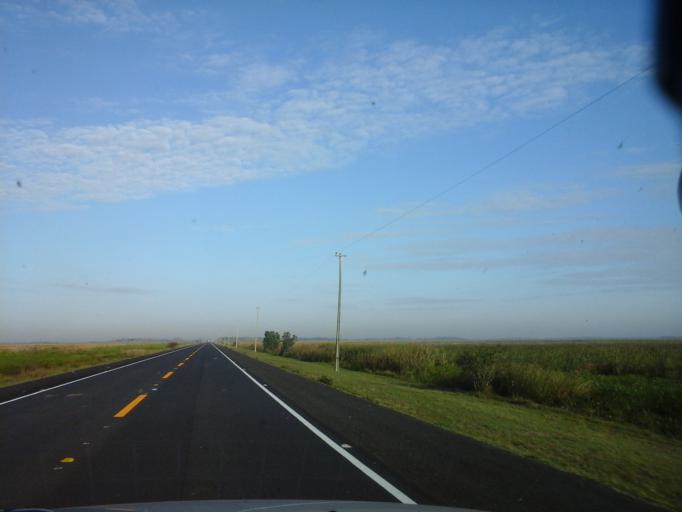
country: PY
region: Neembucu
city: Cerrito
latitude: -26.8889
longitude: -57.6648
